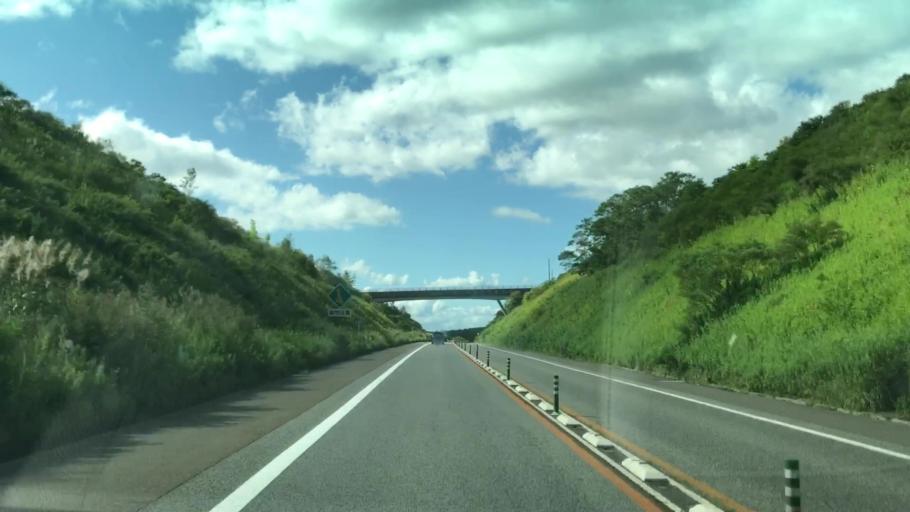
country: JP
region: Hokkaido
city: Muroran
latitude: 42.3959
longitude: 140.9530
